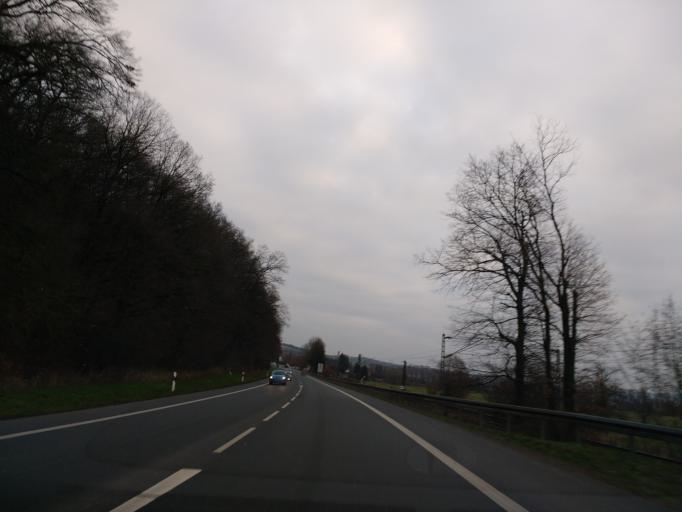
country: DE
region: Hesse
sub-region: Regierungsbezirk Kassel
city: Rotenburg an der Fulda
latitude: 50.9935
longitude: 9.7542
